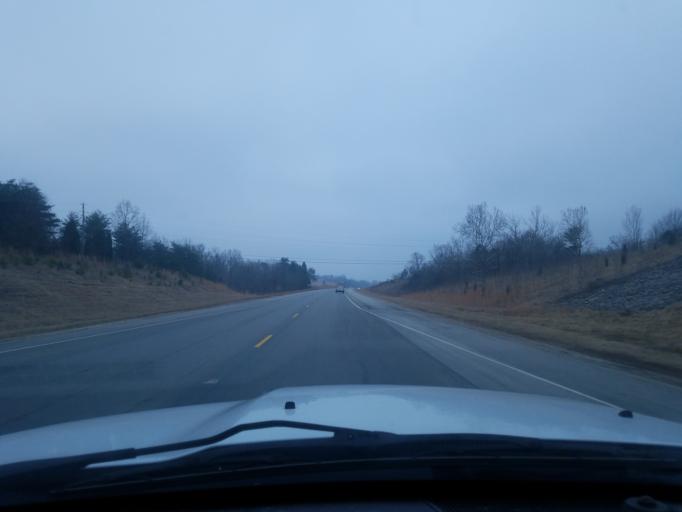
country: US
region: Indiana
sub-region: Perry County
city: Tell City
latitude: 38.0888
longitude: -86.6129
